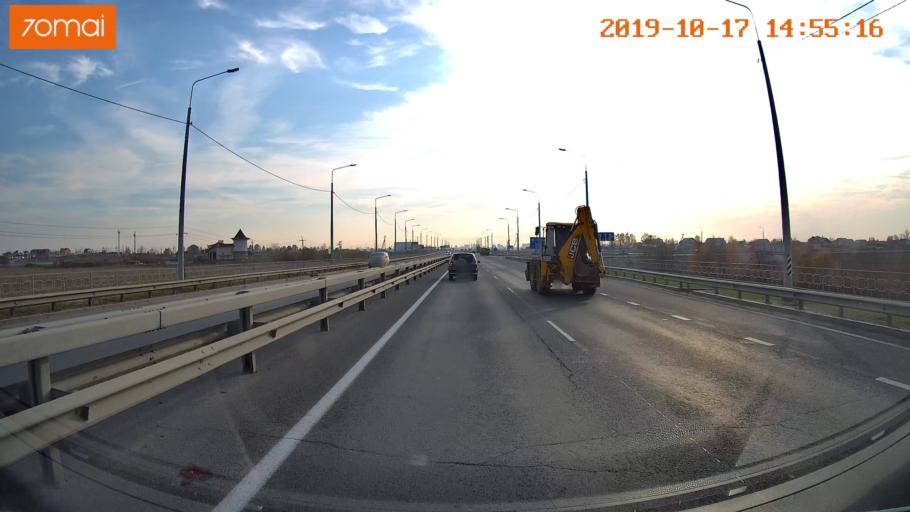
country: RU
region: Rjazan
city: Polyany
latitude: 54.6704
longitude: 39.8264
